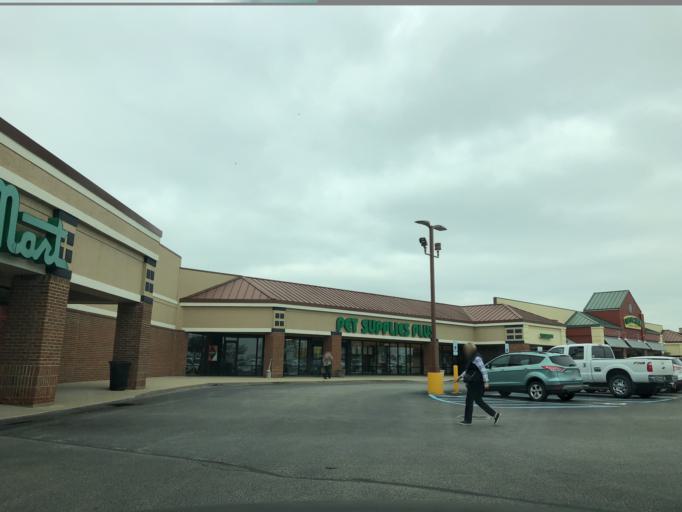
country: US
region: Ohio
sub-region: Hamilton County
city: Sixteen Mile Stand
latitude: 39.2715
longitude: -84.3307
